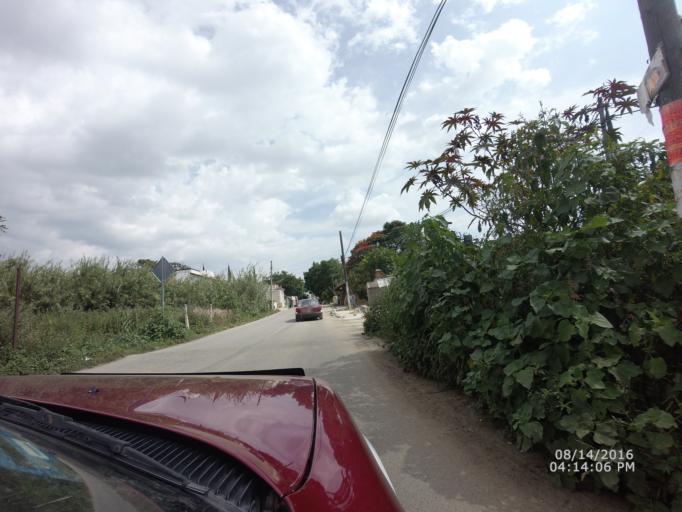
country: MX
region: Oaxaca
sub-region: San Lorenzo Cacaotepec
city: Santiago Etla
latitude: 17.1686
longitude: -96.7851
